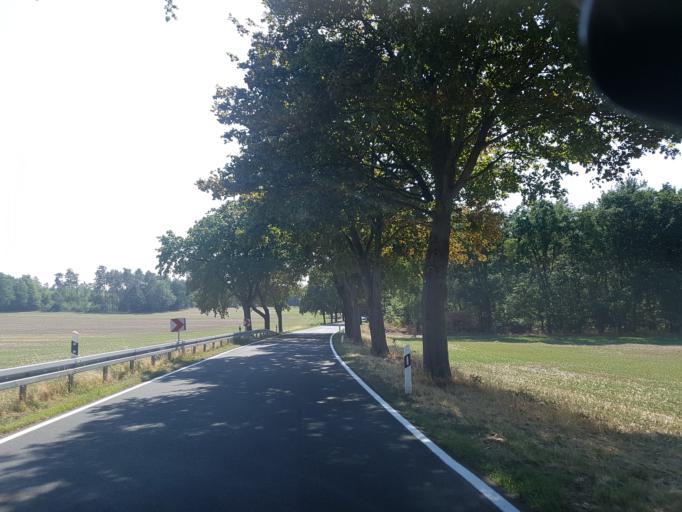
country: DE
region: Brandenburg
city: Wiesenburg
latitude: 52.0516
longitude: 12.3805
